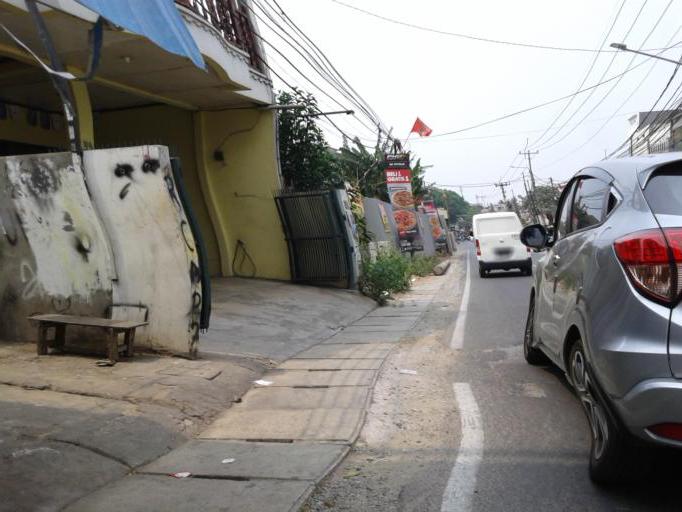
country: ID
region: Banten
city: South Tangerang
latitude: -6.2787
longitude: 106.7621
